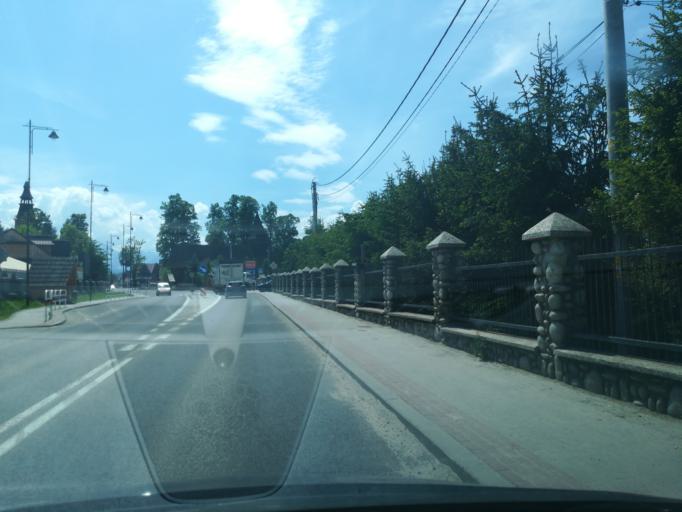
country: PL
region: Lesser Poland Voivodeship
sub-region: Powiat tatrzanski
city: Bialka Tatrzanska
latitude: 49.3900
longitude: 20.1049
